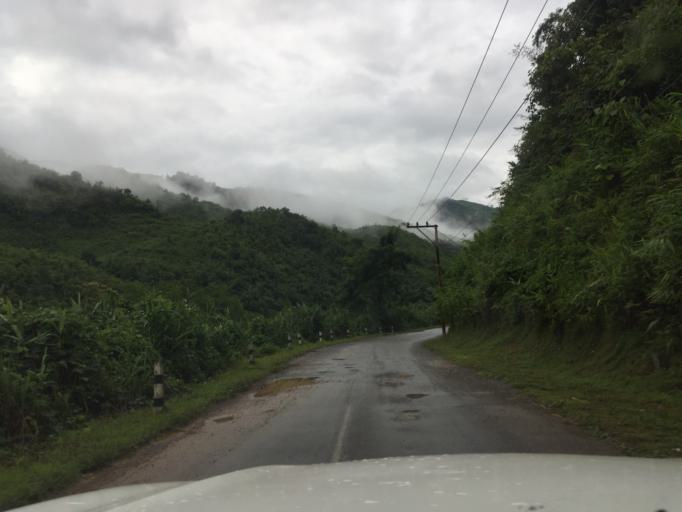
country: LA
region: Oudomxai
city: Muang La
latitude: 20.9316
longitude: 102.2066
